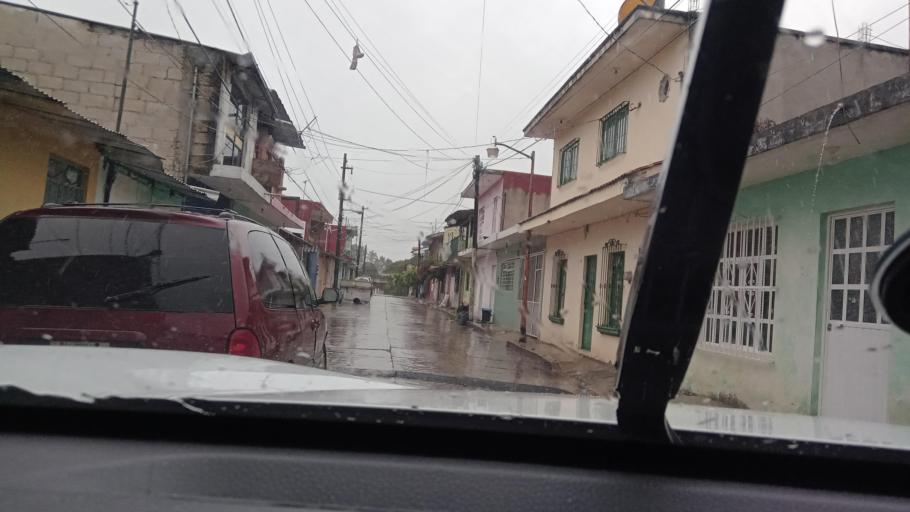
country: MX
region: Veracruz
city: Coatepec
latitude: 19.4555
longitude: -96.9689
